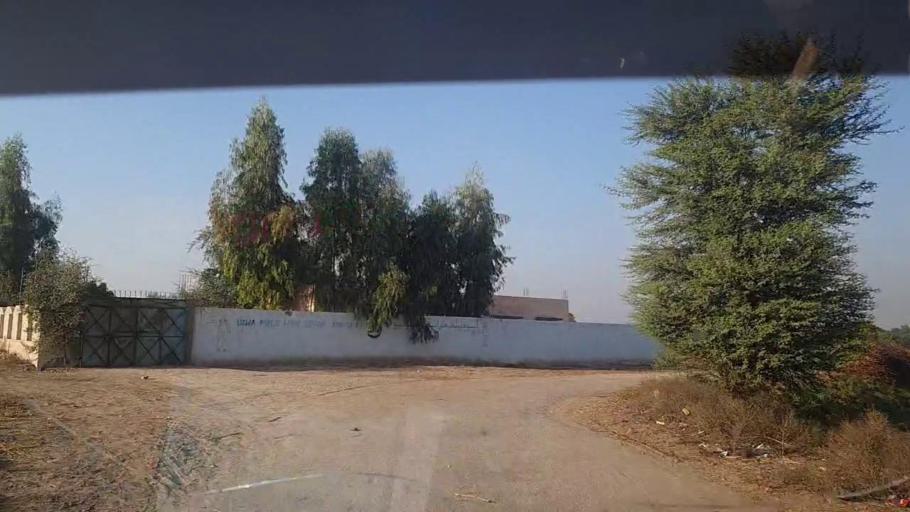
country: PK
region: Sindh
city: Sobhadero
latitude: 27.3010
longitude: 68.4198
